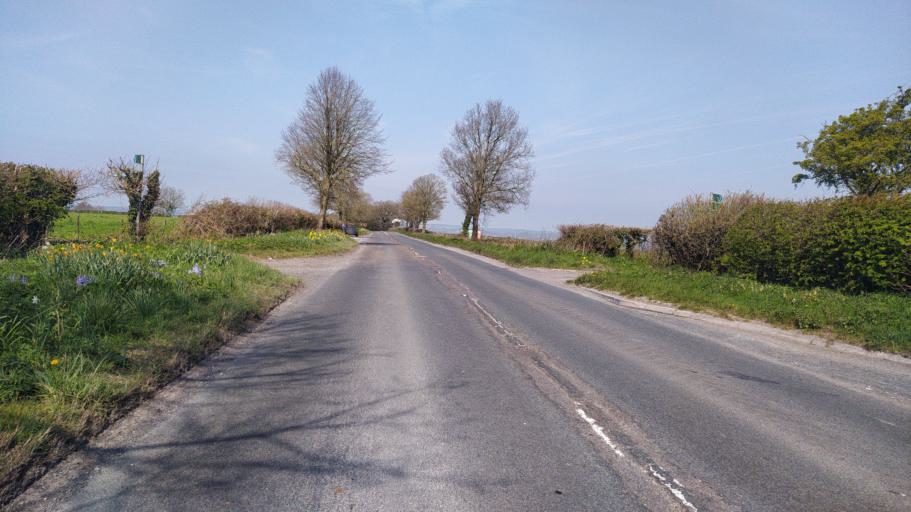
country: GB
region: England
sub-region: Wiltshire
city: Corsley
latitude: 51.2094
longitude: -2.2636
